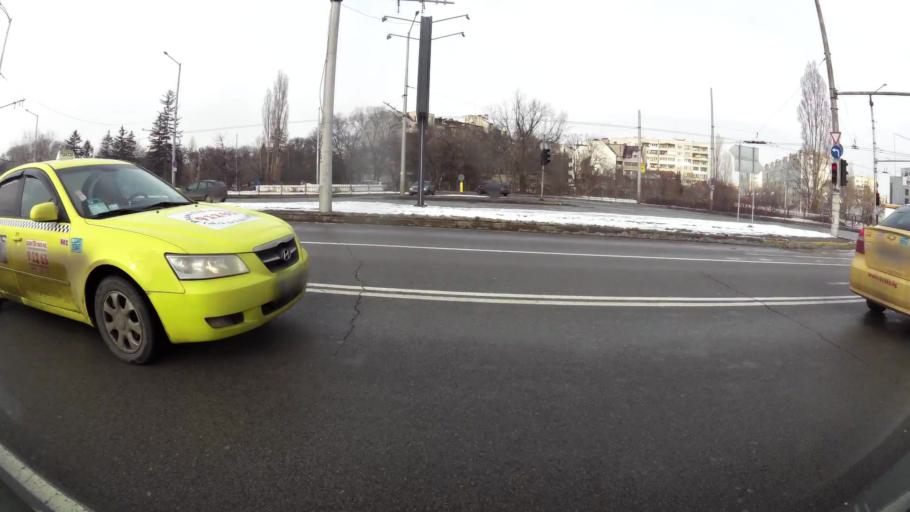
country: BG
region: Sofia-Capital
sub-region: Stolichna Obshtina
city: Sofia
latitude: 42.7017
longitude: 23.3498
